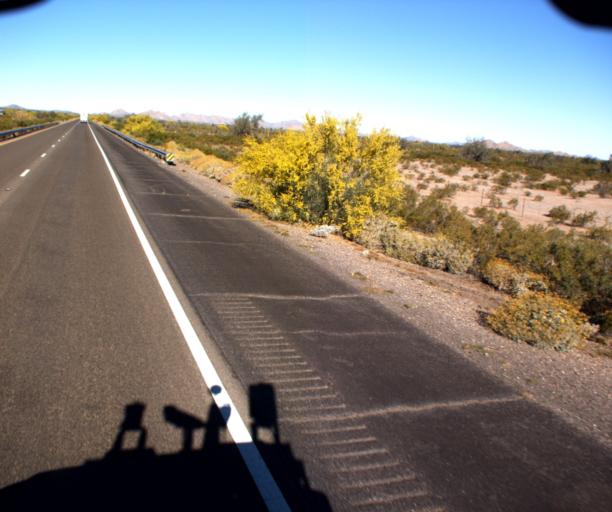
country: US
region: Arizona
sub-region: Pinal County
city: Maricopa
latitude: 32.8302
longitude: -112.0135
